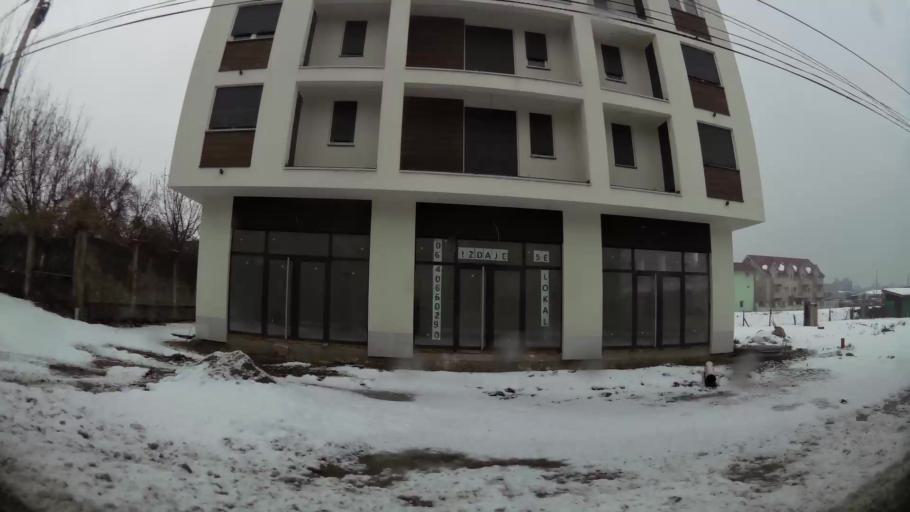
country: RS
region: Central Serbia
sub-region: Belgrade
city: Zemun
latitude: 44.8574
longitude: 20.3566
